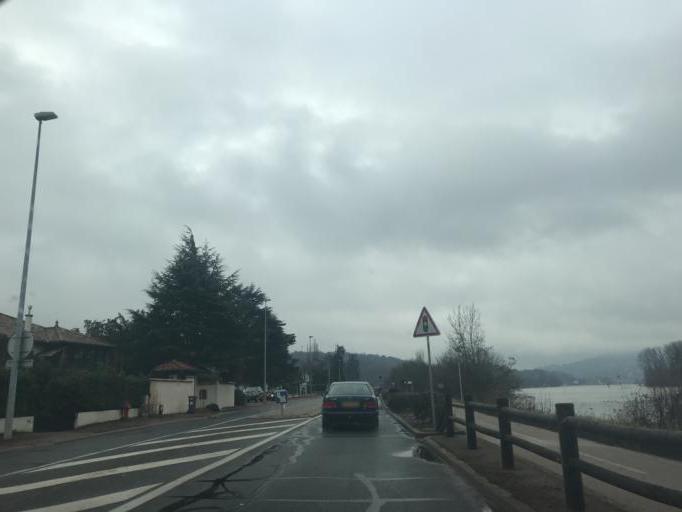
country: FR
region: Rhone-Alpes
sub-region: Departement du Rhone
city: Fleurieu-sur-Saone
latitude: 45.8642
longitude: 4.8402
